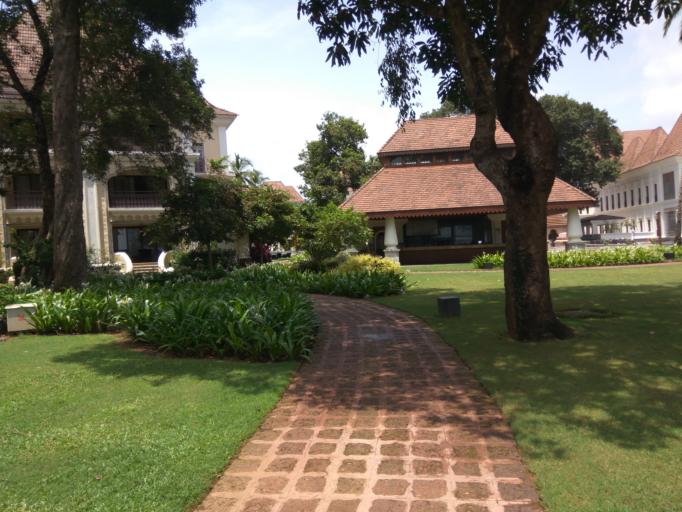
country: IN
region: Goa
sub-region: North Goa
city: Bambolim
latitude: 15.4513
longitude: 73.8505
